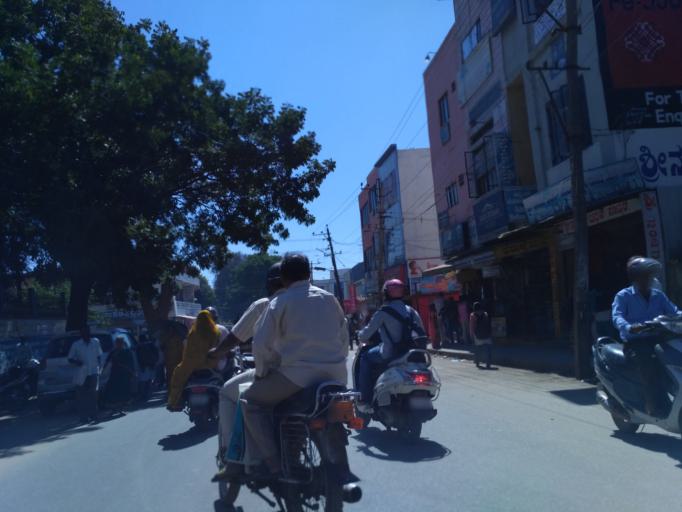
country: IN
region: Karnataka
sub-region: Hassan
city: Hassan
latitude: 13.0045
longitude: 76.1020
